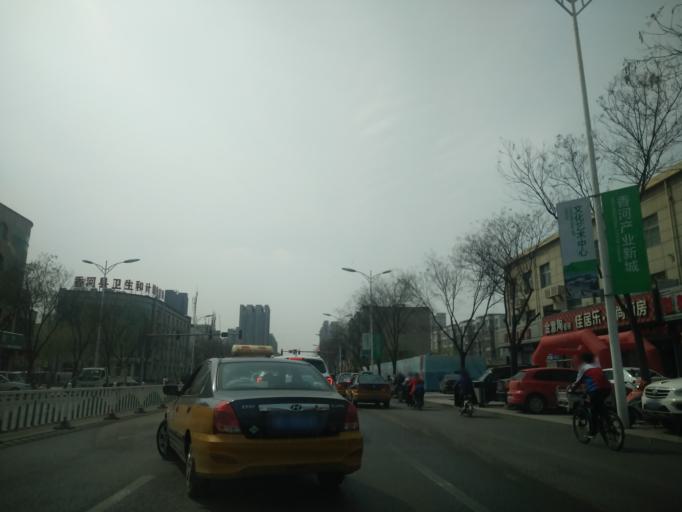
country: CN
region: Beijing
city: Xiji
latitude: 39.7630
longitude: 116.9958
